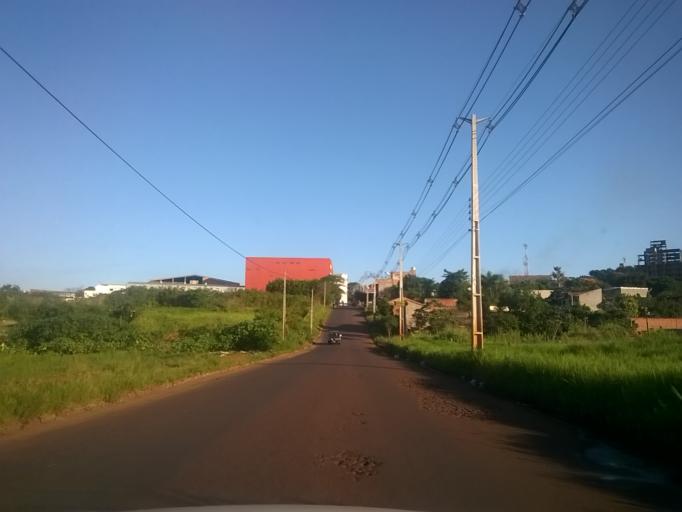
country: PY
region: Alto Parana
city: Ciudad del Este
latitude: -25.5052
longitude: -54.6262
